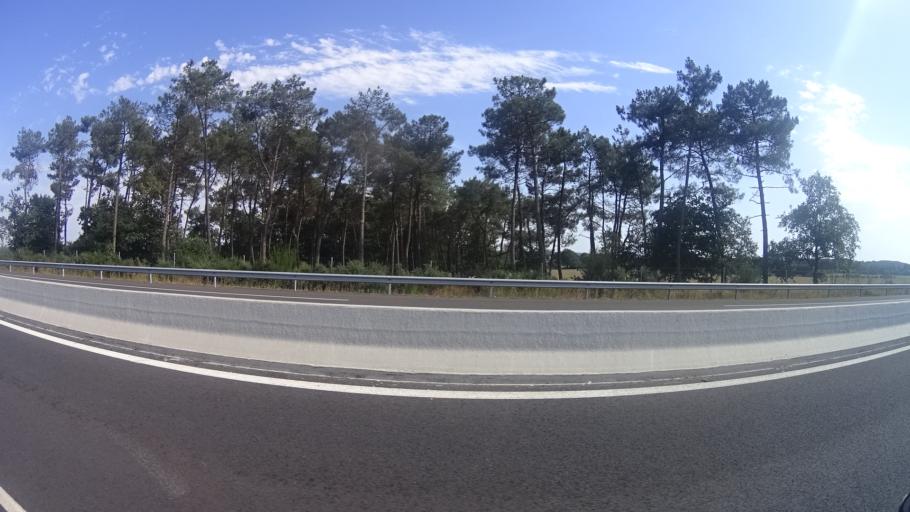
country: FR
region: Brittany
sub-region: Departement du Morbihan
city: Saint-Jean-la-Poterie
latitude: 47.6138
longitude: -2.1286
